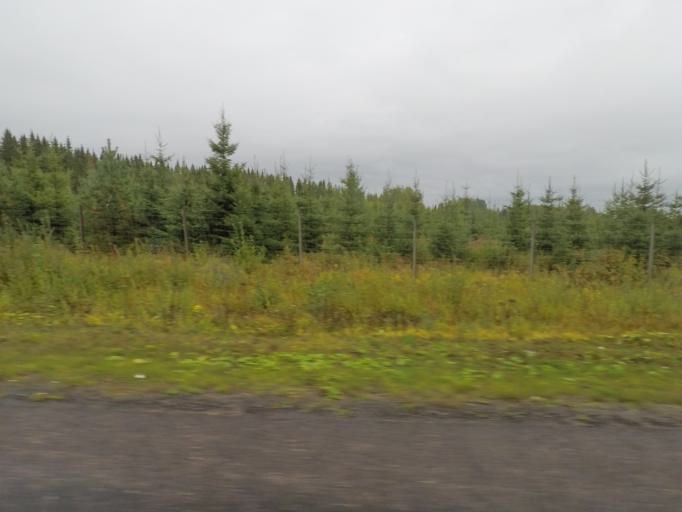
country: FI
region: Northern Savo
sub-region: Varkaus
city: Varkaus
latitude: 62.2718
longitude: 27.8647
